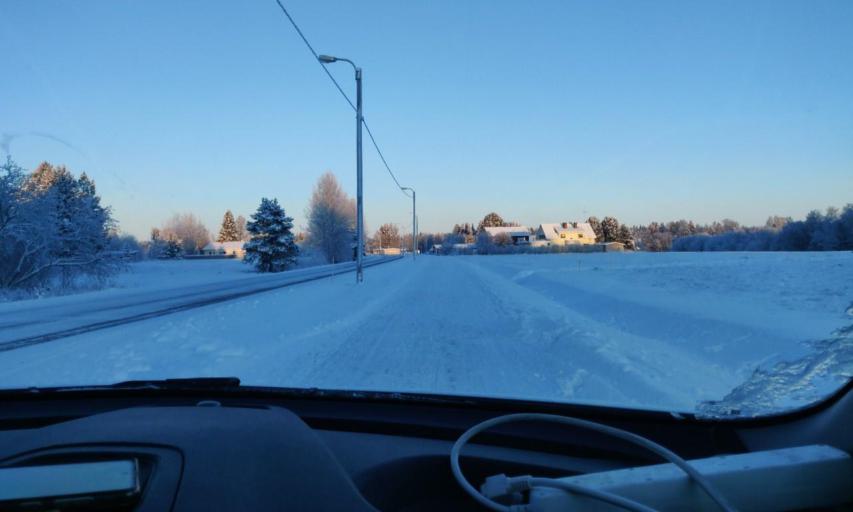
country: FI
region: Northern Ostrobothnia
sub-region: Raahe
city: Siikajoki
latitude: 64.8120
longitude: 24.7679
